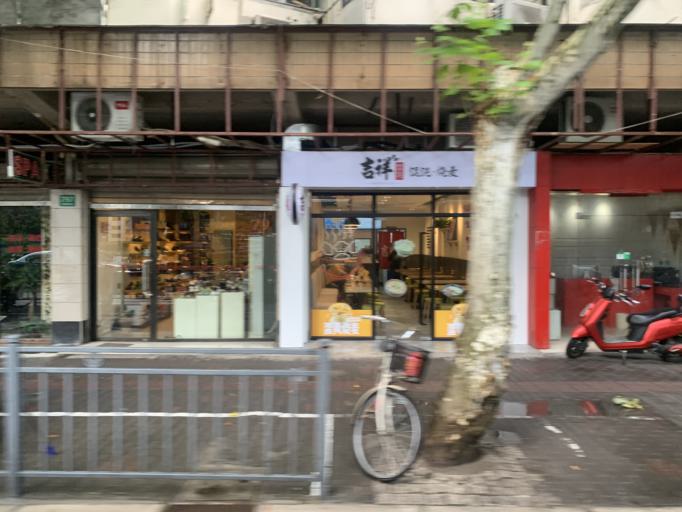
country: CN
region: Shanghai Shi
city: Luwan
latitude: 31.2140
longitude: 121.4731
